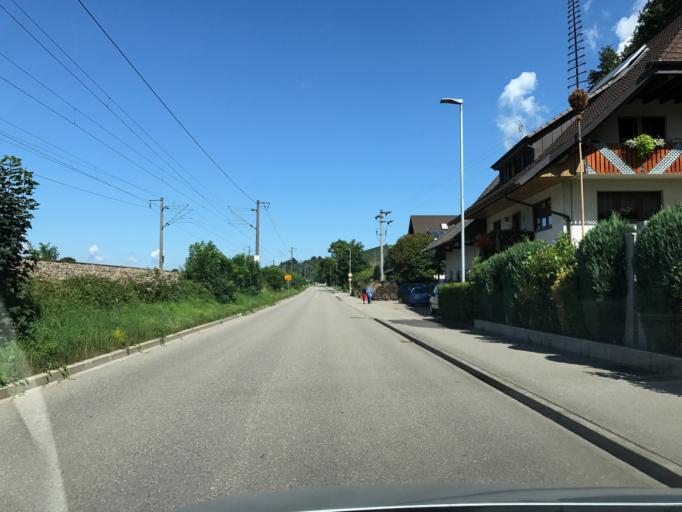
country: DE
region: Hesse
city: Gengenbach
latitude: 48.3948
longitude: 8.0305
